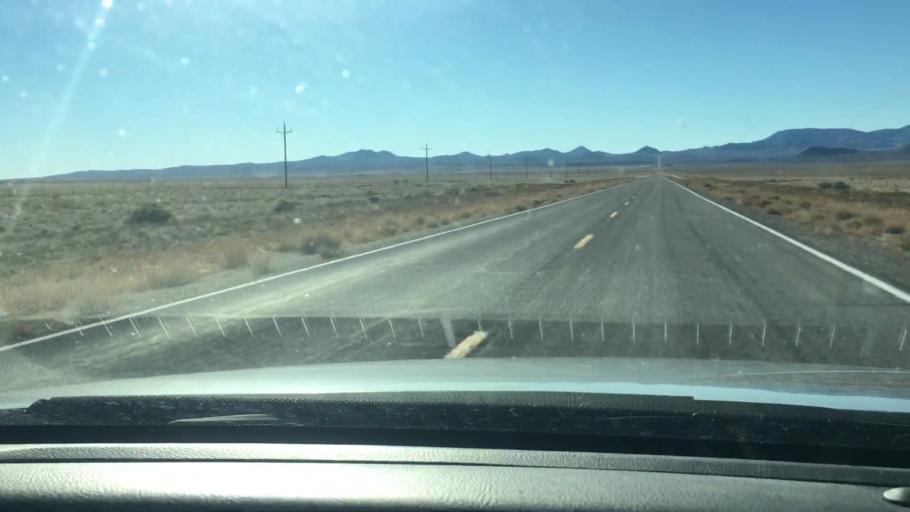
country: US
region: Nevada
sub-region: Nye County
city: Tonopah
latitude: 38.1545
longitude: -116.5414
